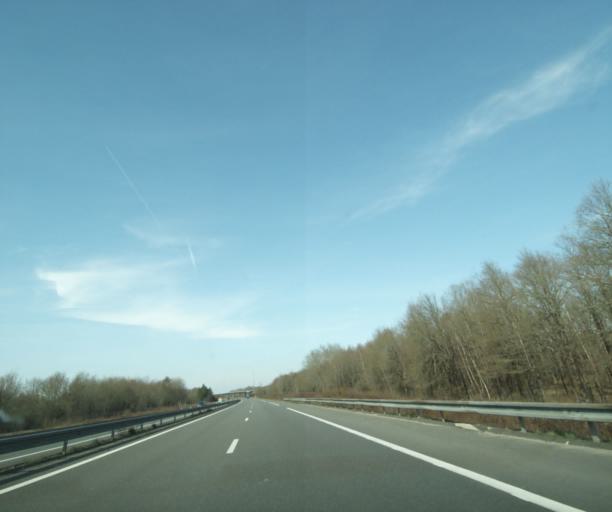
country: FR
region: Centre
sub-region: Departement du Loir-et-Cher
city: Theillay
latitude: 47.3676
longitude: 2.0537
